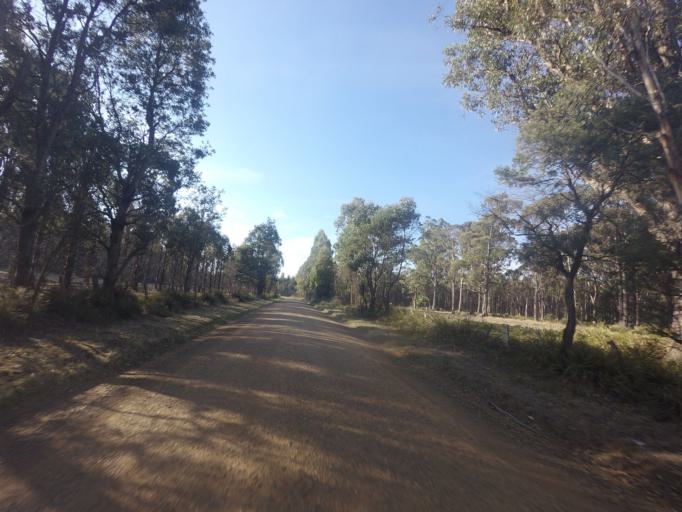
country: AU
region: Tasmania
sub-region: Brighton
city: Bridgewater
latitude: -42.4471
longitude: 147.3856
